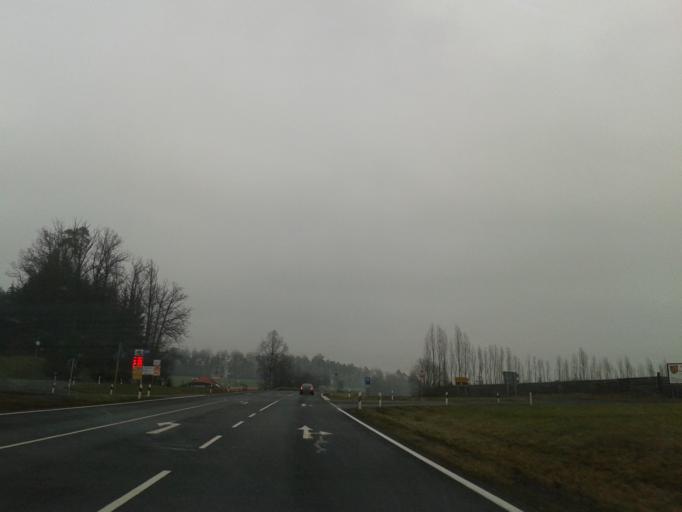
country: DE
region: Bavaria
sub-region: Regierungsbezirk Unterfranken
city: Burgpreppach
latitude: 50.1403
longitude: 10.6368
